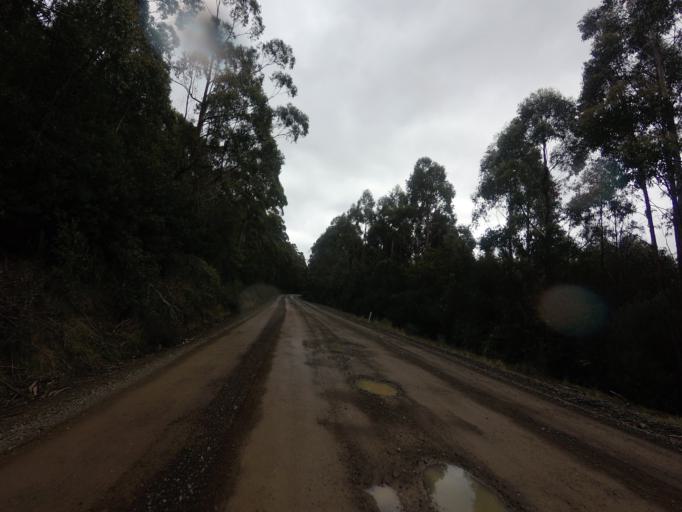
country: AU
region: Tasmania
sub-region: Huon Valley
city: Geeveston
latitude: -43.4761
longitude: 146.8923
